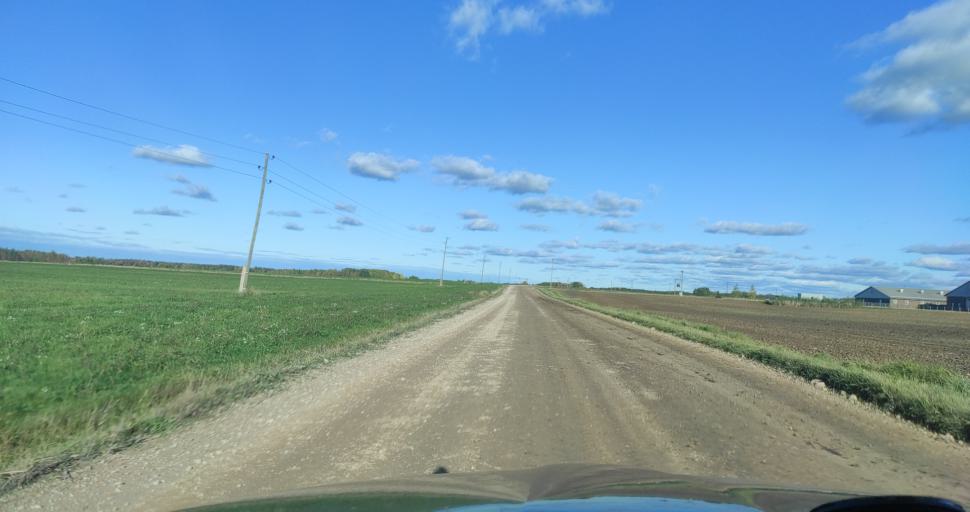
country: LV
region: Aizpute
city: Aizpute
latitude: 56.7685
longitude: 21.4676
